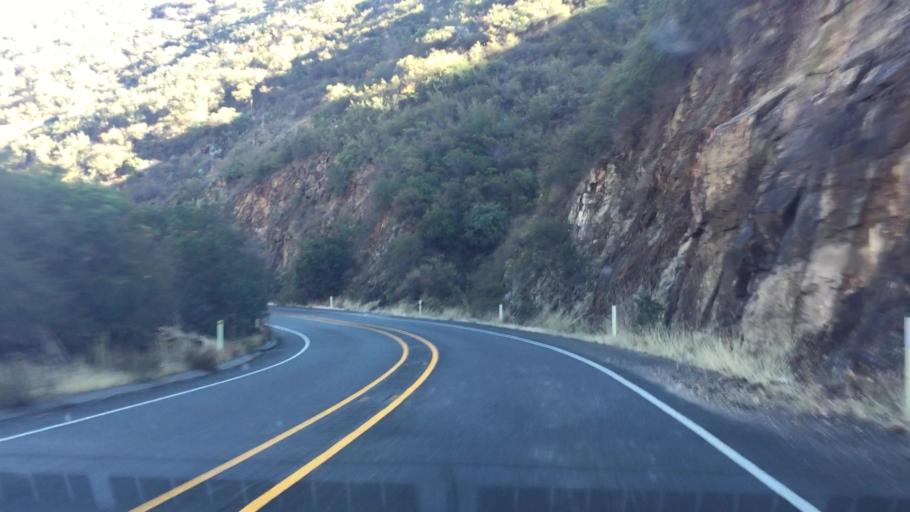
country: US
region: California
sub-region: Orange County
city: Coto De Caza
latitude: 33.5917
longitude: -117.4709
